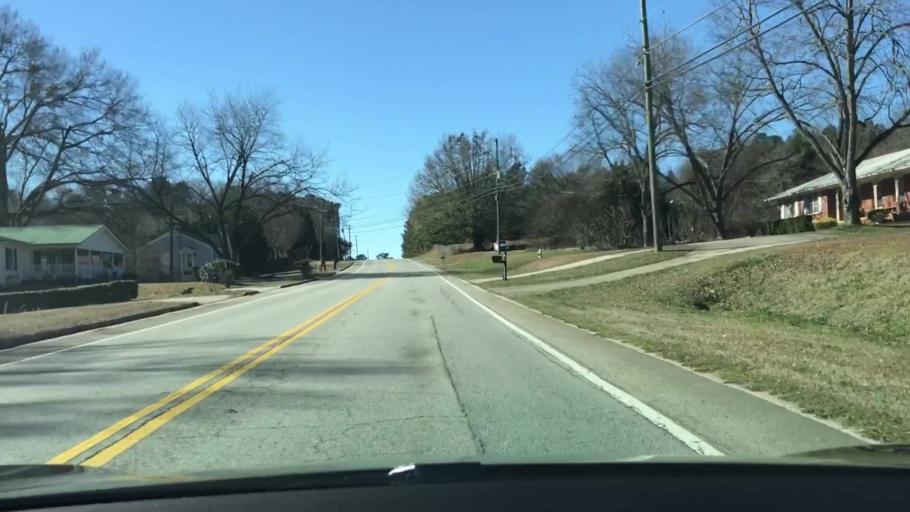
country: US
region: Georgia
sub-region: Gwinnett County
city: Buford
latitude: 34.1418
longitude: -84.0148
